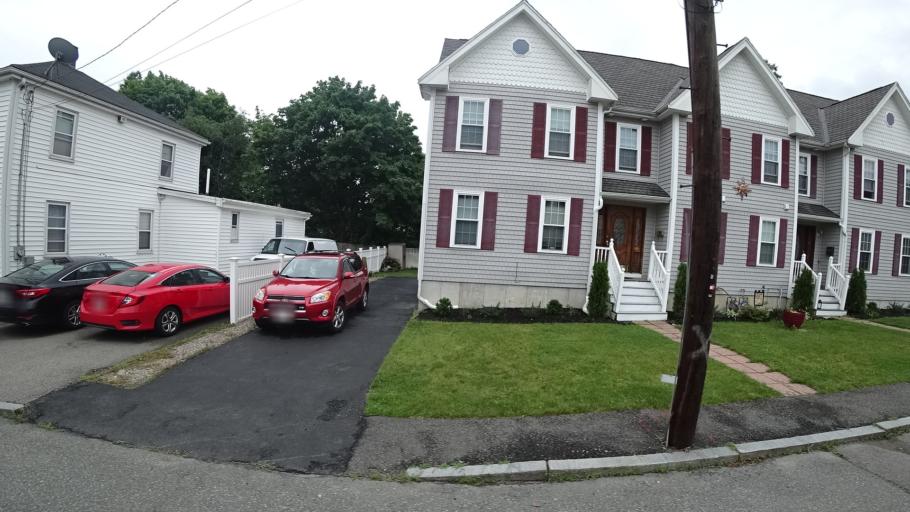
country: US
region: Massachusetts
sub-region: Norfolk County
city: Dedham
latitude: 42.2435
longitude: -71.1436
